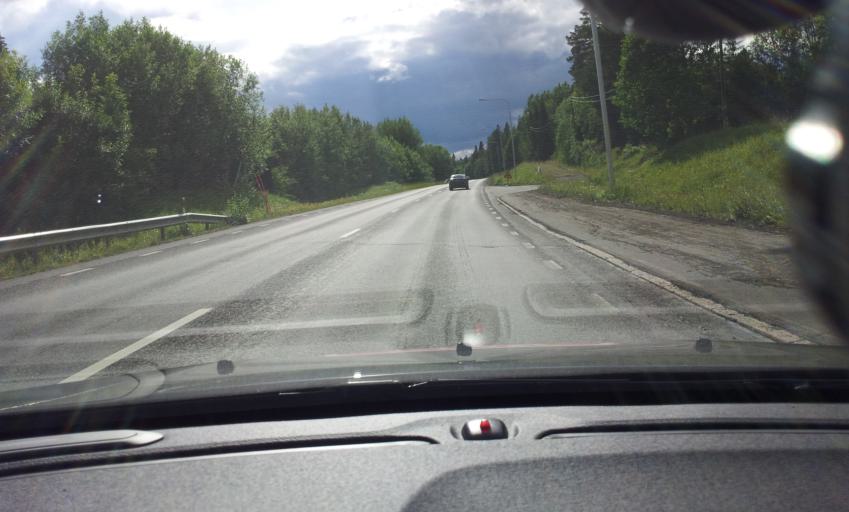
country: SE
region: Jaemtland
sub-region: Are Kommun
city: Jarpen
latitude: 63.3389
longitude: 13.4395
